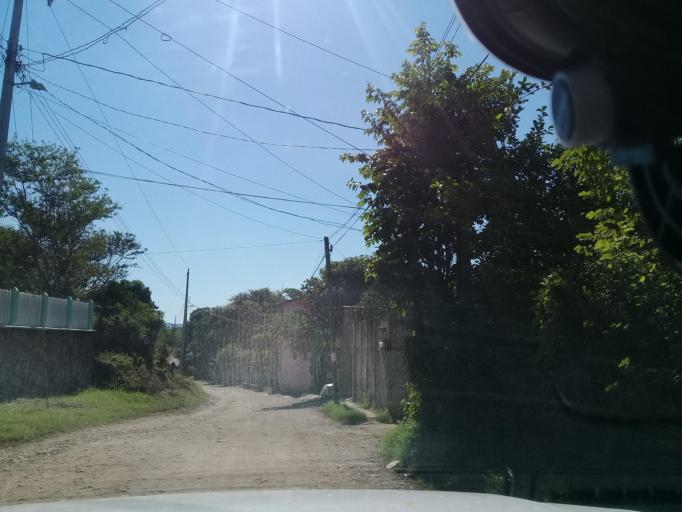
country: MX
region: Hidalgo
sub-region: Huejutla de Reyes
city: Huejutla de Reyes
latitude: 21.1629
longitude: -98.4180
